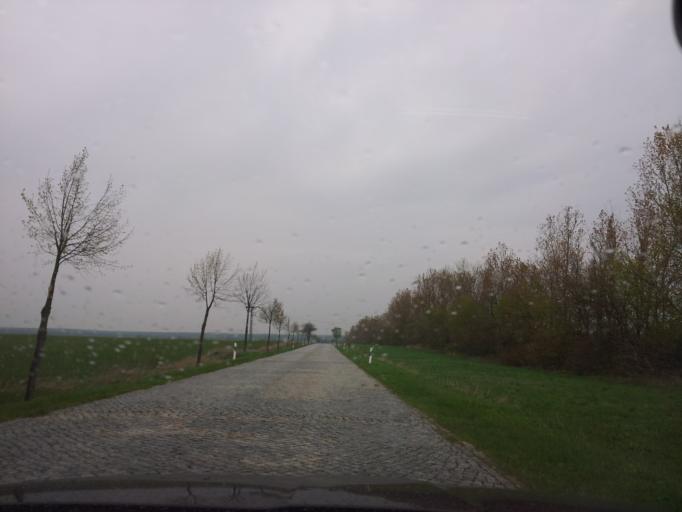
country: DE
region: Brandenburg
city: Niedergorsdorf
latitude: 52.0029
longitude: 12.9138
